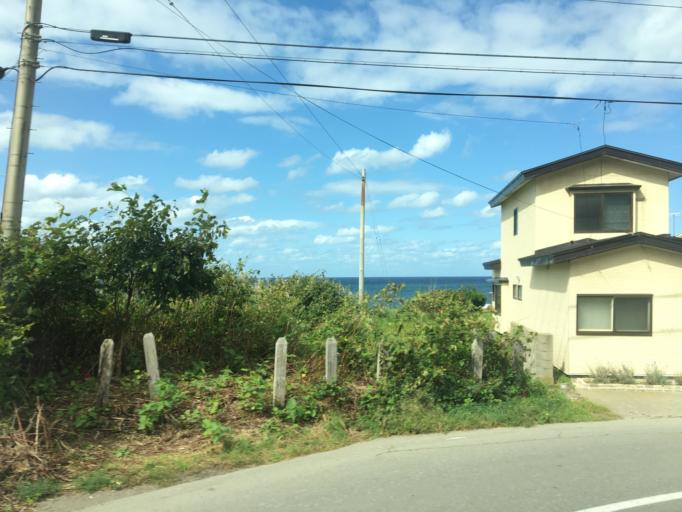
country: JP
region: Aomori
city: Shimokizukuri
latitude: 40.7683
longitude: 140.1686
